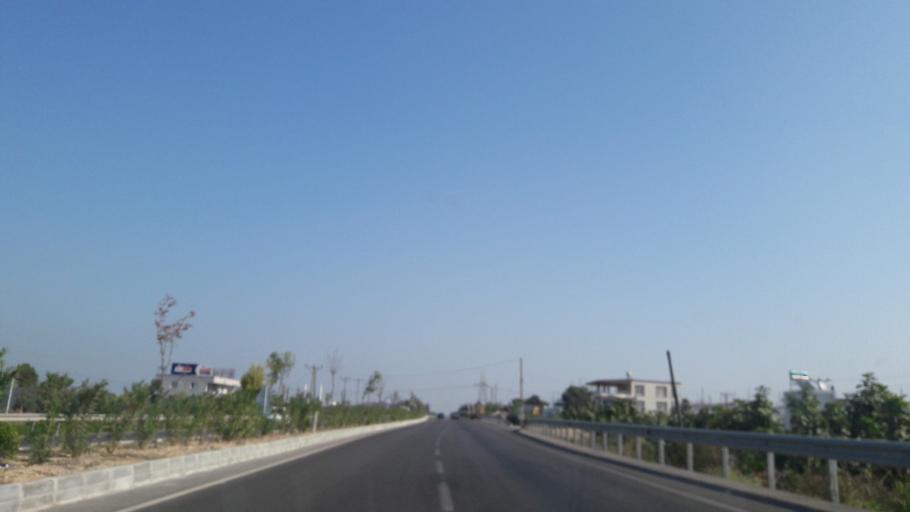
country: TR
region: Adana
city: Yakapinar
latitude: 37.1030
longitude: 35.5079
